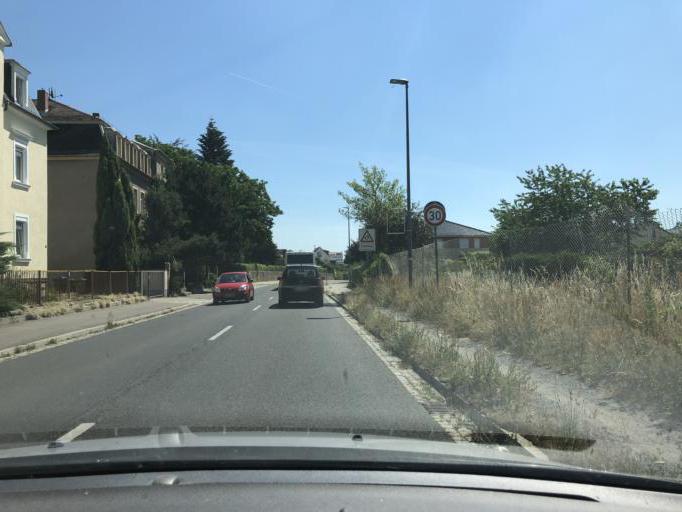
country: DE
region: Saxony
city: Coswig
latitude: 51.1103
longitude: 13.6035
